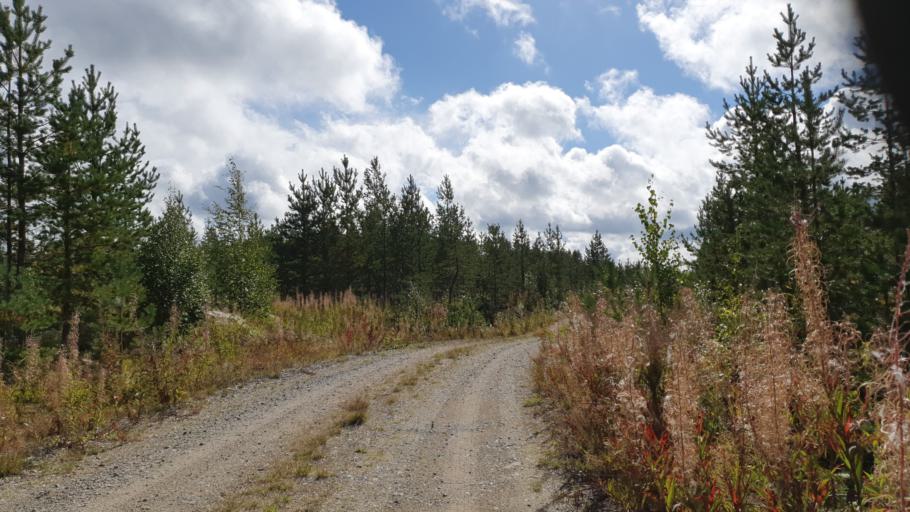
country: FI
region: Kainuu
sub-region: Kehys-Kainuu
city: Kuhmo
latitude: 64.1490
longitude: 29.3888
